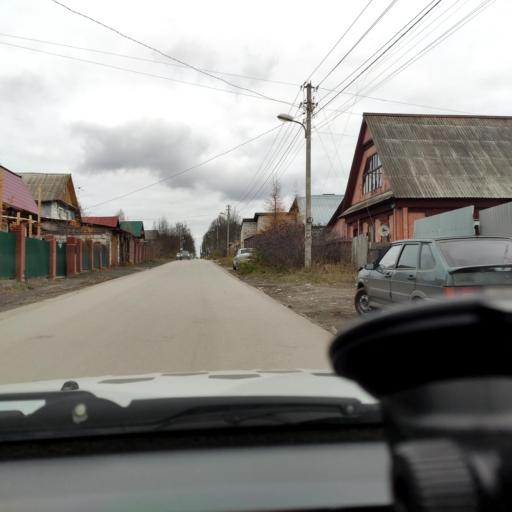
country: RU
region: Perm
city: Kondratovo
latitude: 58.0474
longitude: 56.1202
